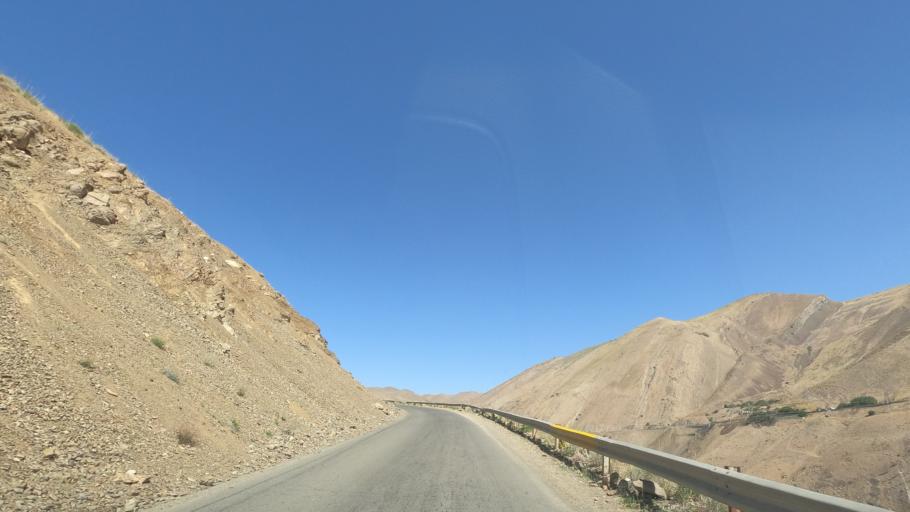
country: IR
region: Alborz
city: Karaj
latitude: 35.9402
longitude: 51.0839
